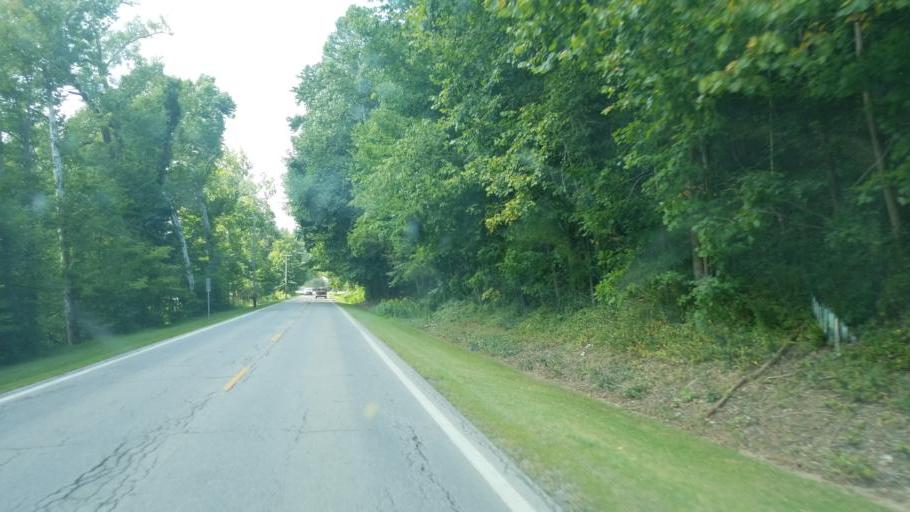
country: US
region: Ohio
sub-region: Sandusky County
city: Bellville
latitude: 40.6222
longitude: -82.5054
